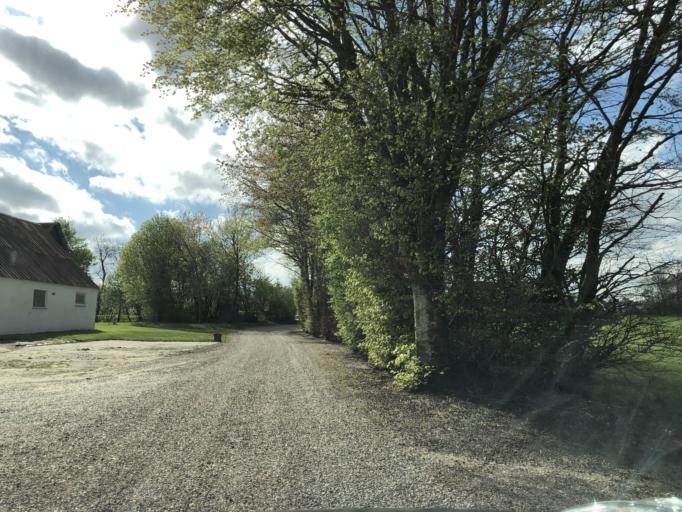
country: DK
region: Central Jutland
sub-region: Herning Kommune
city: Avlum
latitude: 56.2967
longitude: 8.7426
